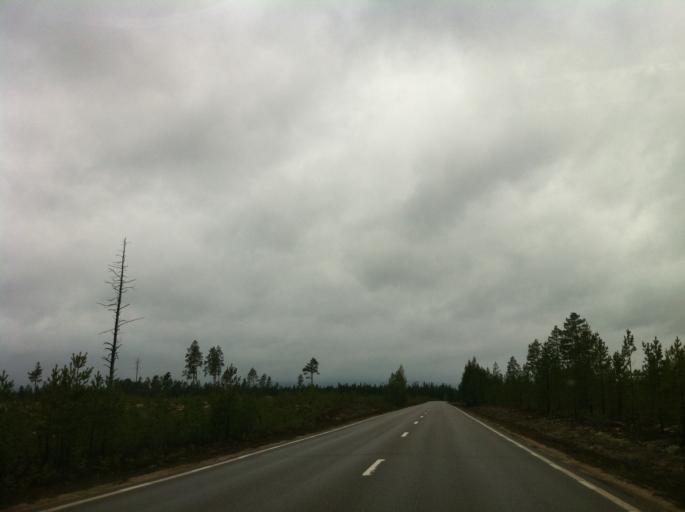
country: SE
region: Jaemtland
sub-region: Harjedalens Kommun
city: Sveg
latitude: 62.1363
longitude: 14.0325
